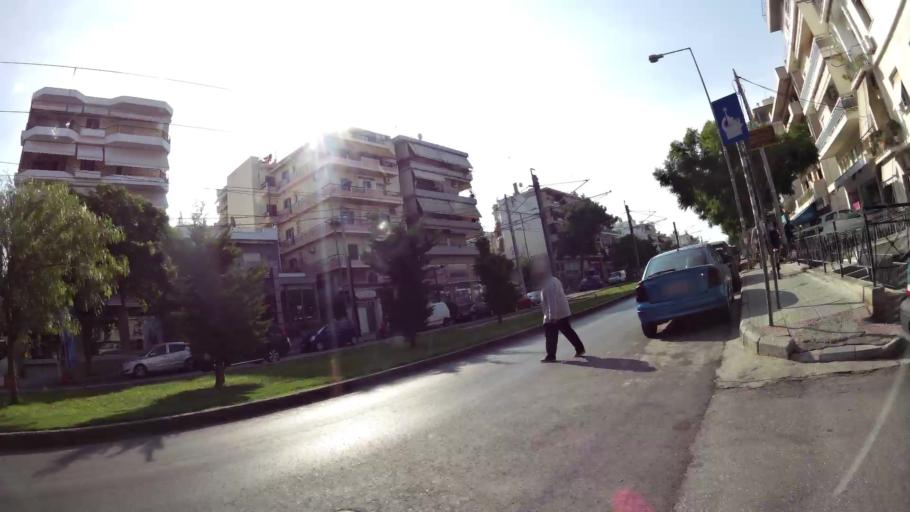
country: GR
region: Attica
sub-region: Nomarchia Athinas
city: Nea Smyrni
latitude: 37.9352
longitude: 23.7115
